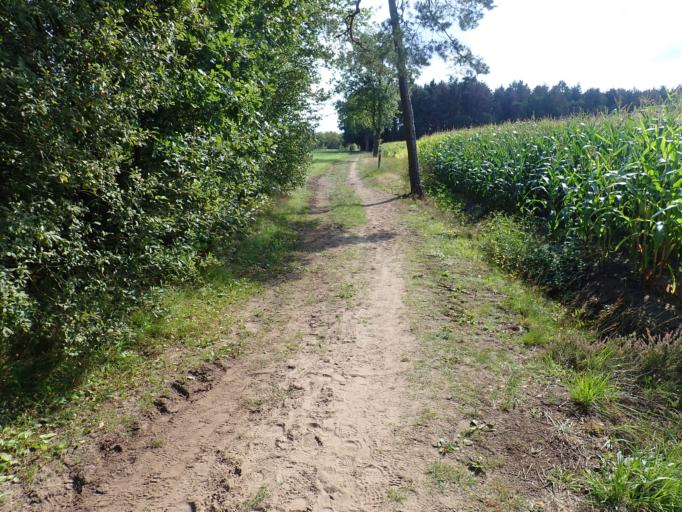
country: BE
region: Flanders
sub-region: Provincie Antwerpen
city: Beerse
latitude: 51.2902
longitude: 4.8175
